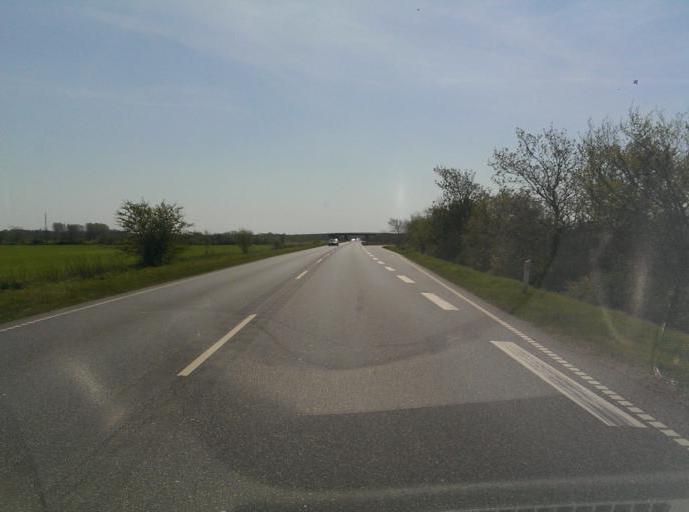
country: DK
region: South Denmark
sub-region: Esbjerg Kommune
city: Bramming
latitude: 55.4094
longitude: 8.7207
